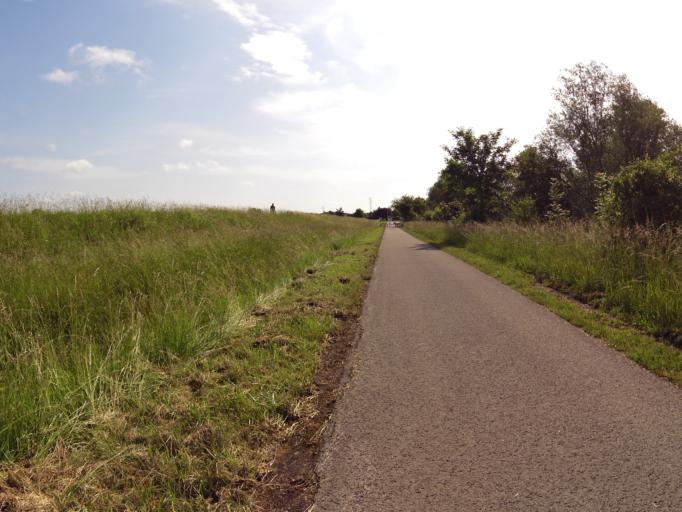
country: FR
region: Champagne-Ardenne
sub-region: Departement de l'Aube
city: Saint-Julien-les-Villas
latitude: 48.2662
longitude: 4.1335
